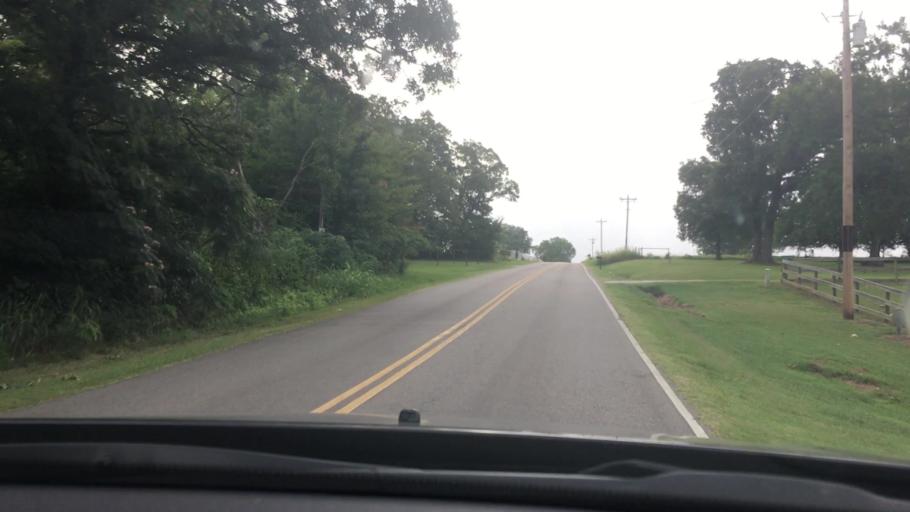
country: US
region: Oklahoma
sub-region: Pontotoc County
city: Ada
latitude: 34.8106
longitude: -96.6315
